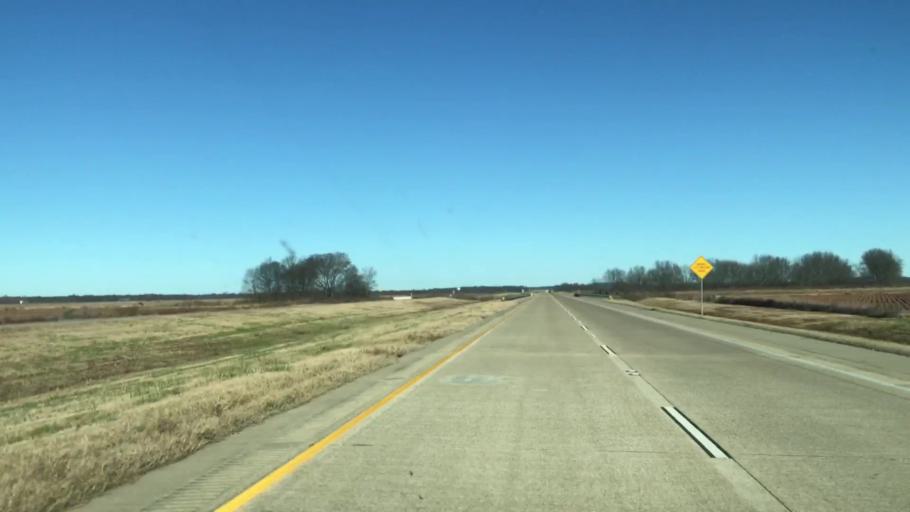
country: US
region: Louisiana
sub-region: Caddo Parish
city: Oil City
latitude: 32.7178
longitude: -93.8680
